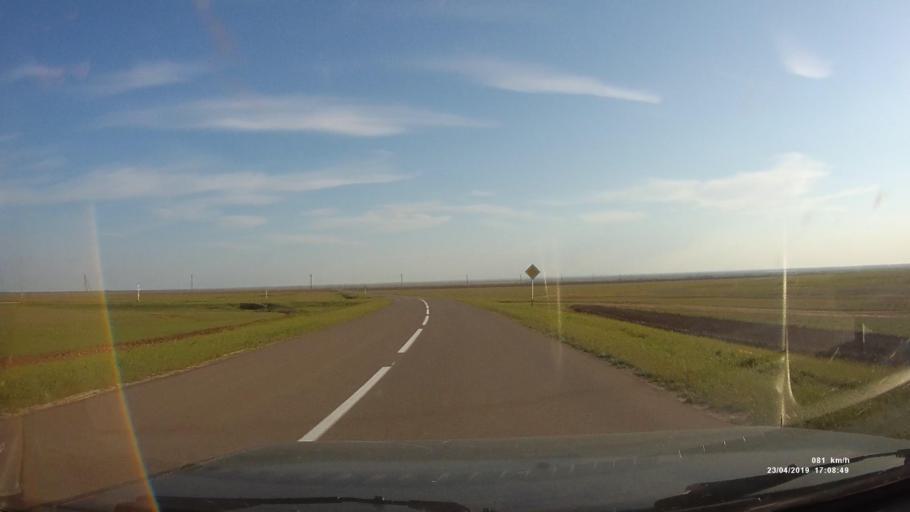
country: RU
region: Kalmykiya
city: Priyutnoye
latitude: 46.2667
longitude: 43.4846
